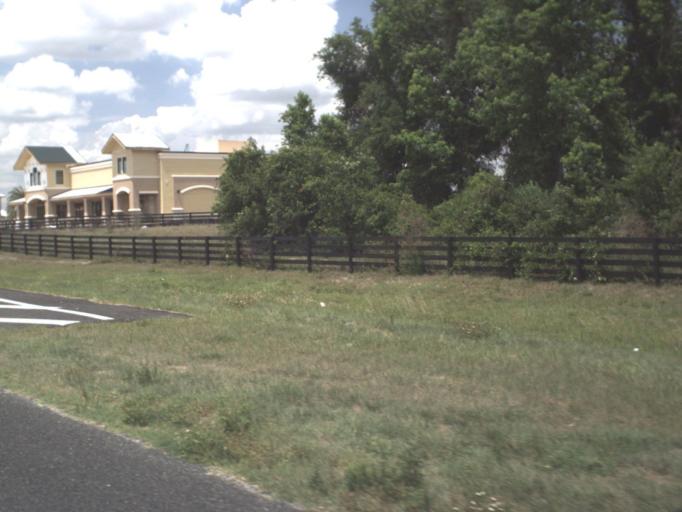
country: US
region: Florida
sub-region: Lake County
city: Fruitland Park
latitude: 28.8227
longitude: -81.9635
